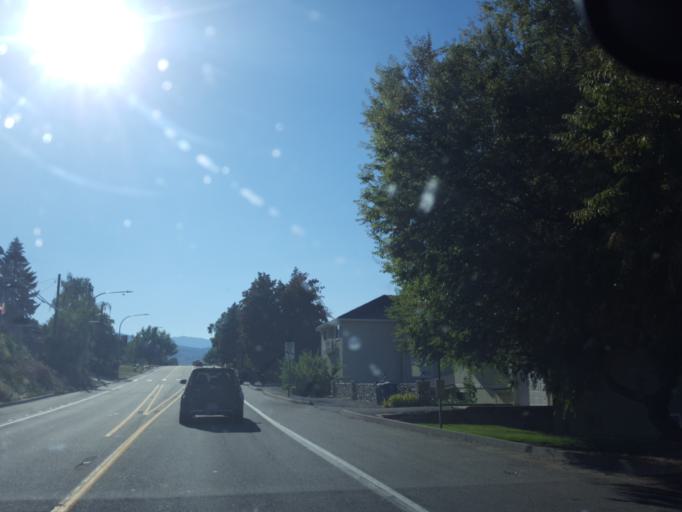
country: US
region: Washington
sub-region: Chelan County
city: Chelan
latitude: 47.8352
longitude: -120.0465
